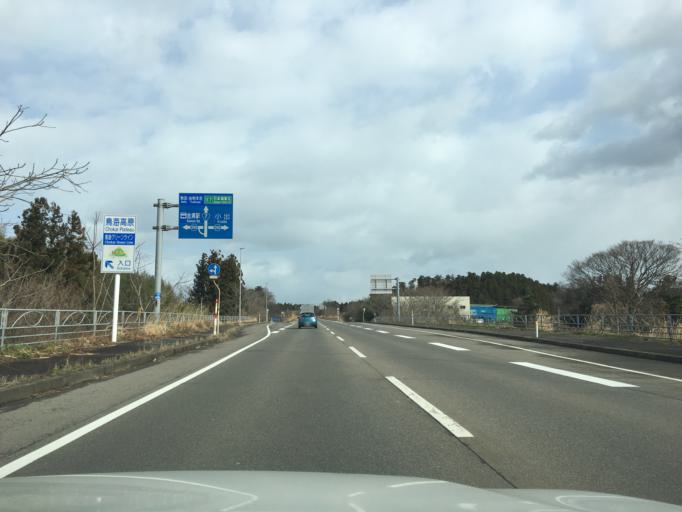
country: JP
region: Yamagata
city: Yuza
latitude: 39.2542
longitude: 139.9269
